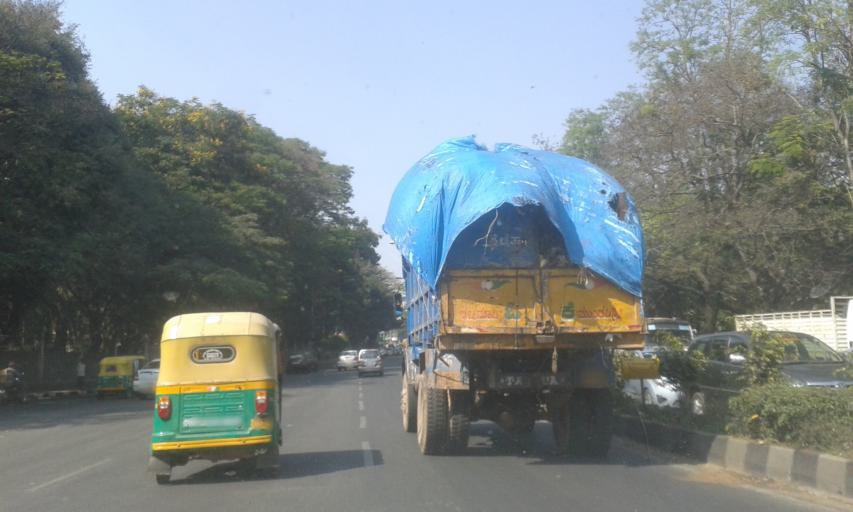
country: IN
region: Karnataka
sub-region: Bangalore Urban
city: Bangalore
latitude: 13.0000
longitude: 77.5841
